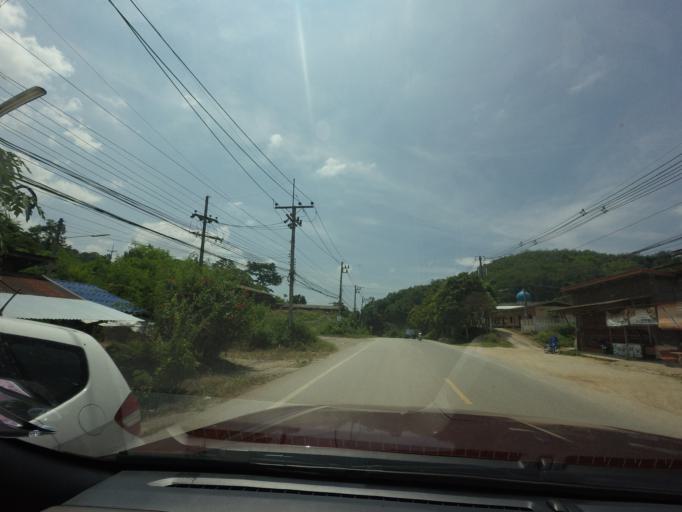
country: TH
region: Yala
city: Betong
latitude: 5.8069
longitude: 101.0786
